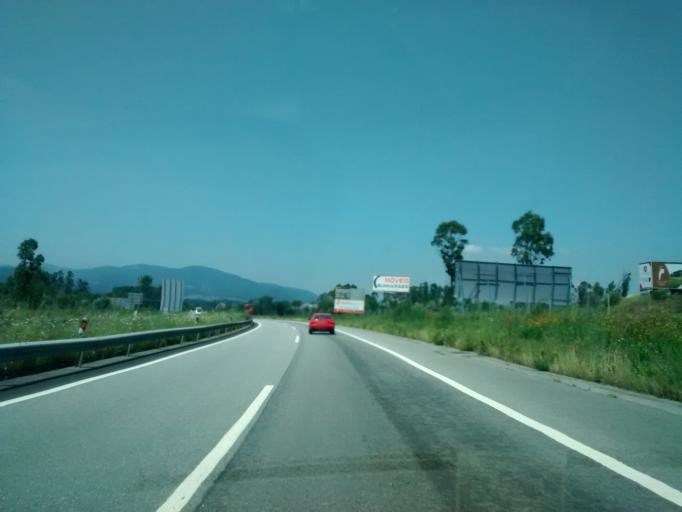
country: PT
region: Viana do Castelo
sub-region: Valenca
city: Valenza
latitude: 41.9975
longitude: -8.6429
